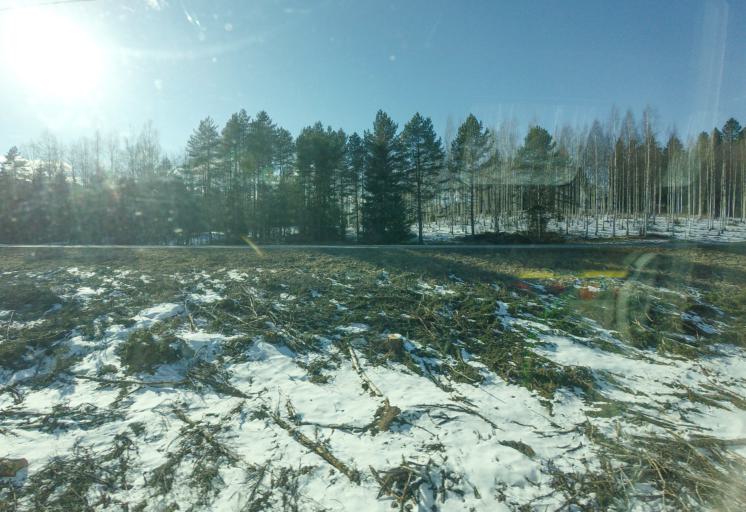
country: FI
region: South Karelia
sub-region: Imatra
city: Parikkala
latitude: 61.5175
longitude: 29.5126
